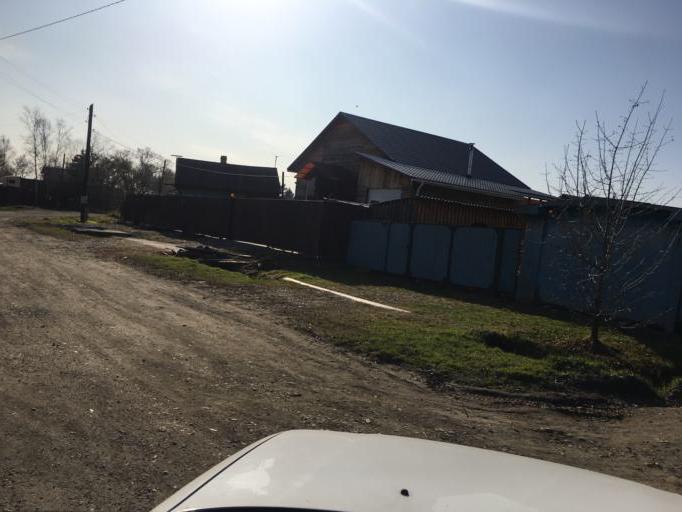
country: RU
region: Primorskiy
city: Dal'nerechensk
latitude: 45.9275
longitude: 133.7259
